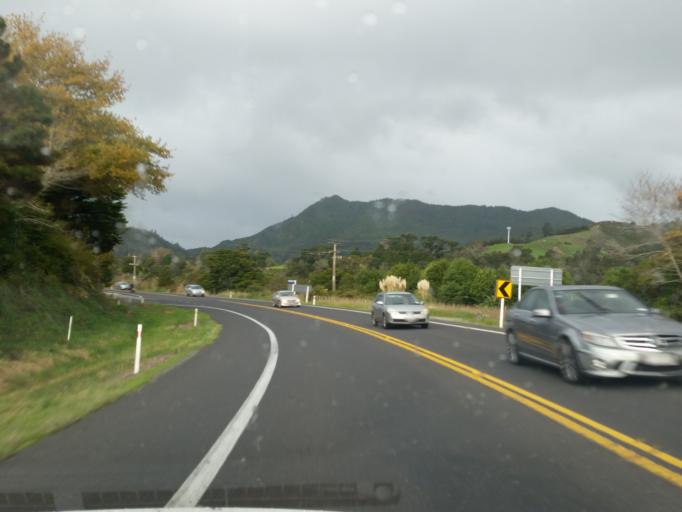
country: NZ
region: Waikato
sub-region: Hauraki District
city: Paeroa
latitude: -37.4109
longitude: 175.7057
